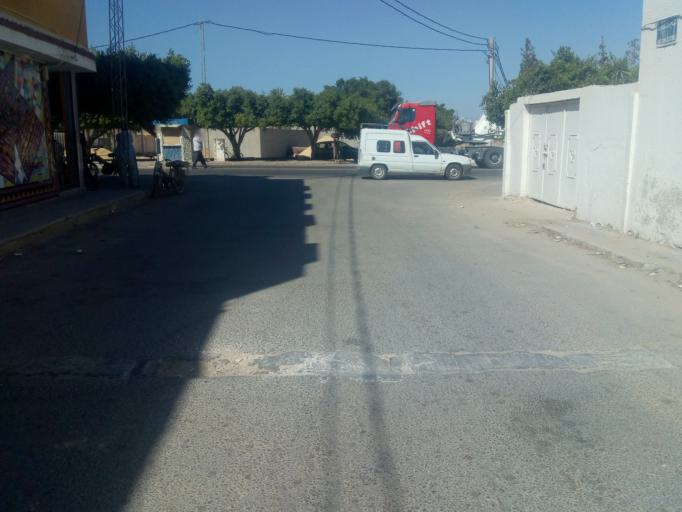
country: TN
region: Qabis
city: Gabes
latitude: 33.6200
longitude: 10.2833
